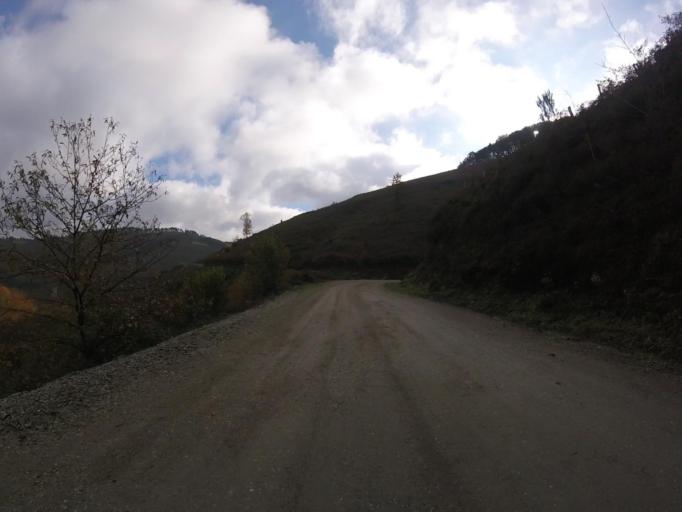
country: ES
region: Navarre
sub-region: Provincia de Navarra
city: Goizueta
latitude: 43.2124
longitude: -1.8413
